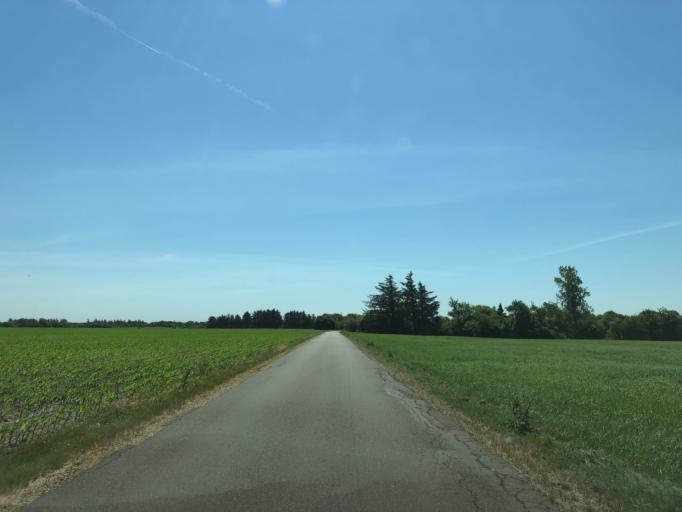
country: DK
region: Central Jutland
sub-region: Holstebro Kommune
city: Ulfborg
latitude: 56.3944
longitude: 8.4278
